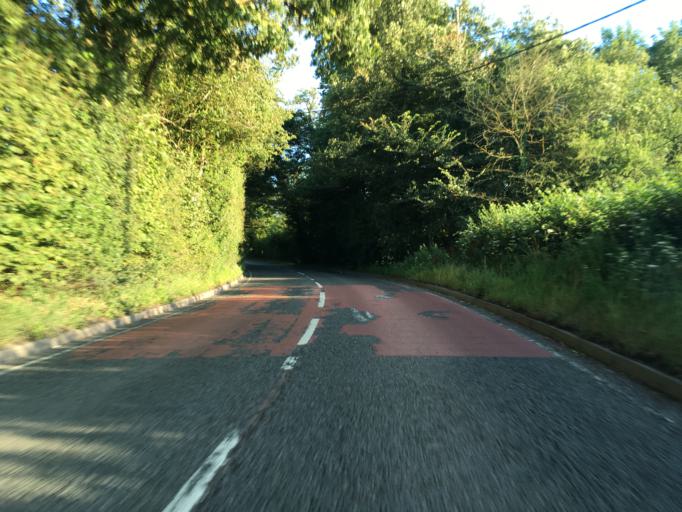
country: GB
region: England
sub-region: Hampshire
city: Tadley
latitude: 51.3792
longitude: -1.1525
